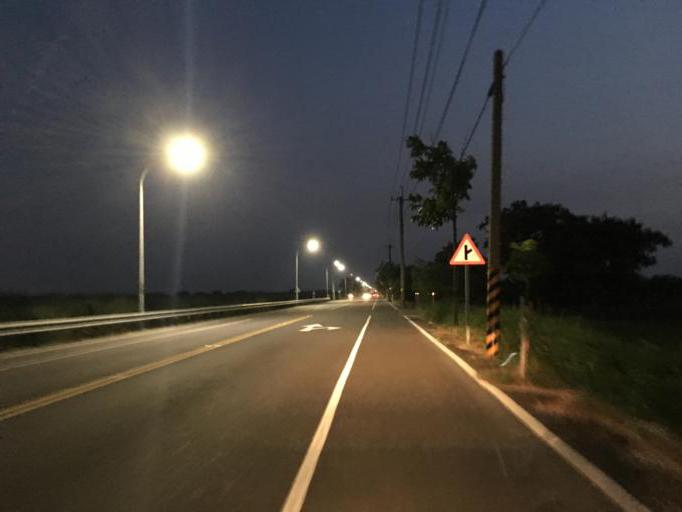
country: TW
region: Taiwan
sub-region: Chiayi
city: Taibao
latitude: 23.5296
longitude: 120.3256
